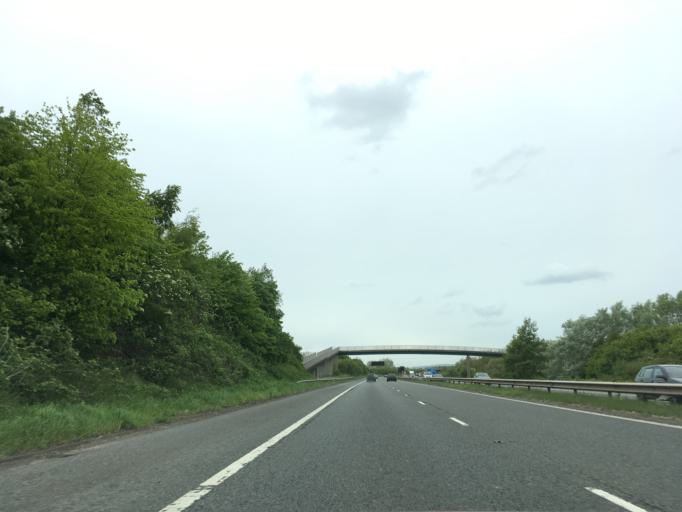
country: GB
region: England
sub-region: South Gloucestershire
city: Severn Beach
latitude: 51.5605
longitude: -2.6543
